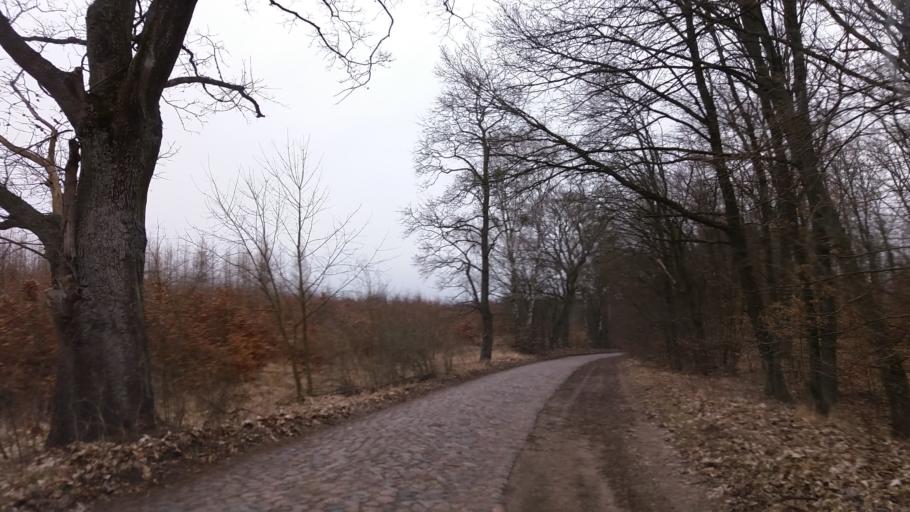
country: PL
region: West Pomeranian Voivodeship
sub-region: Powiat choszczenski
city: Choszczno
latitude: 53.1894
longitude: 15.3416
